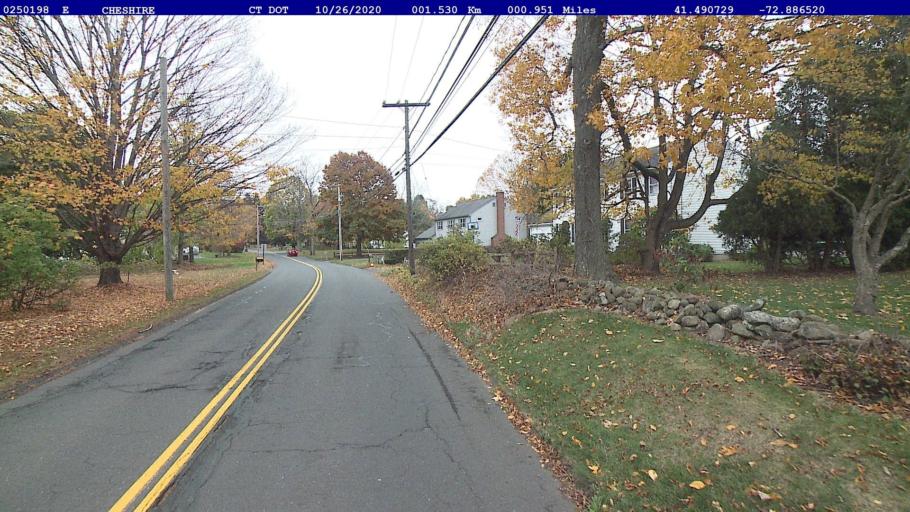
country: US
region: Connecticut
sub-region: New Haven County
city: Cheshire
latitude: 41.4907
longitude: -72.8865
